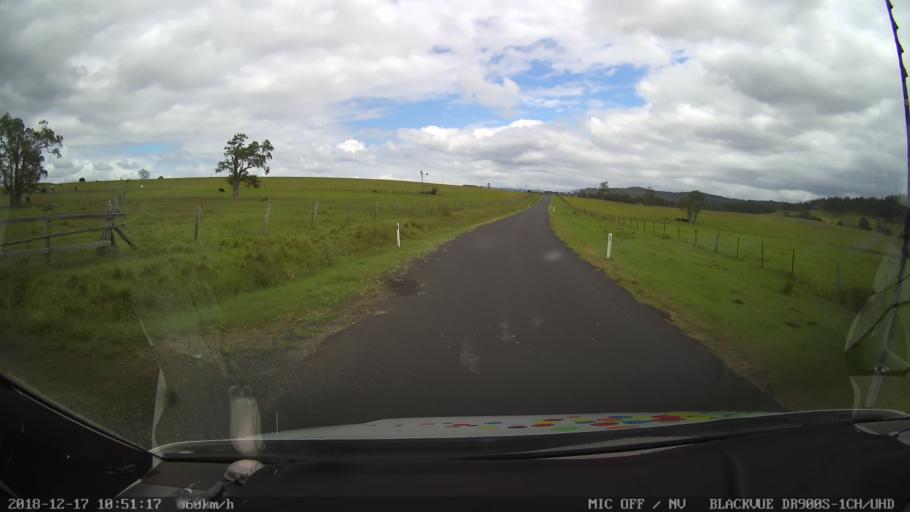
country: AU
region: New South Wales
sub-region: Tenterfield Municipality
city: Carrolls Creek
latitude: -28.8530
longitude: 152.5678
